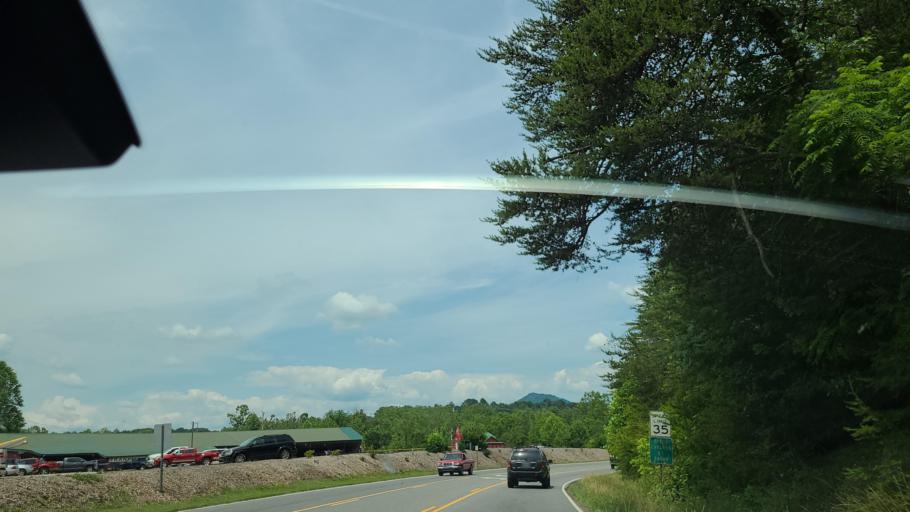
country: US
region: North Carolina
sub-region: Macon County
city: Franklin
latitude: 35.1763
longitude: -83.3658
